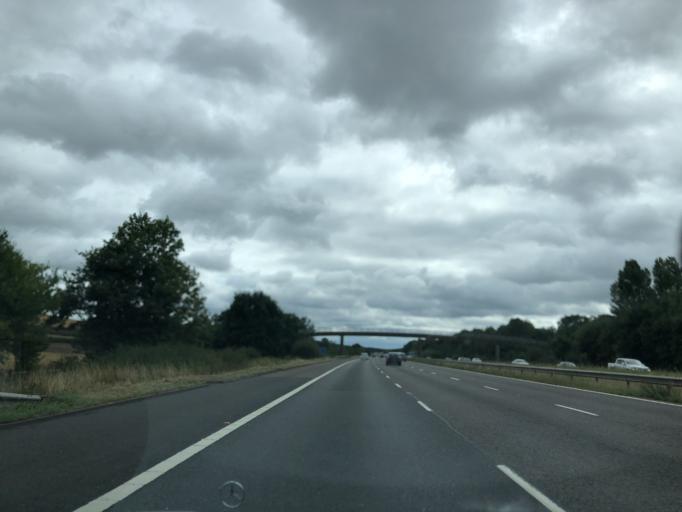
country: GB
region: England
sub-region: Oxfordshire
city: Hanwell
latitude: 52.1102
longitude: -1.3628
